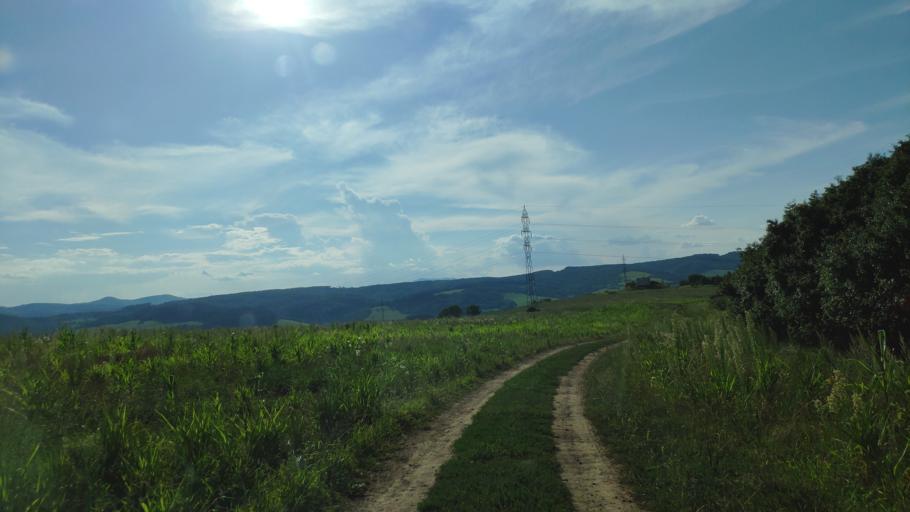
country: SK
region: Presovsky
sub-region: Okres Presov
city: Presov
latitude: 48.9136
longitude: 21.2721
